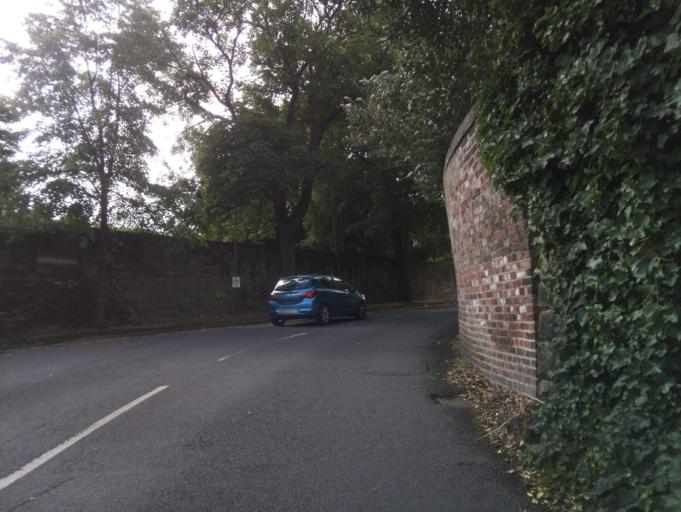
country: GB
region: England
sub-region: Derbyshire
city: Ilkeston
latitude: 52.9387
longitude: -1.3082
